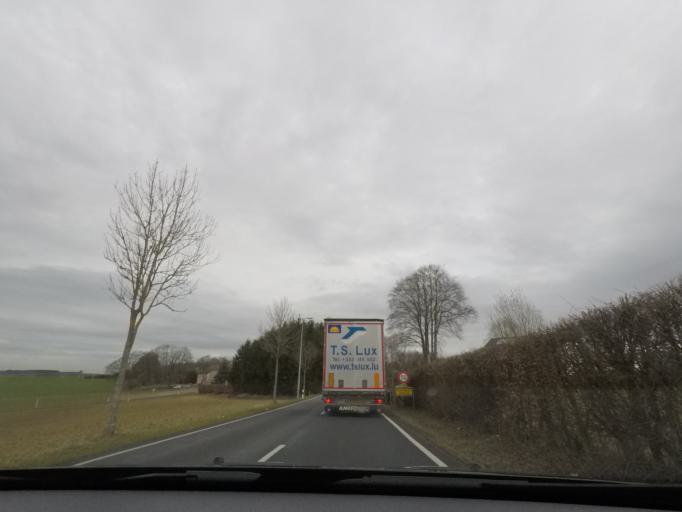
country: LU
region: Diekirch
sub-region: Canton de Wiltz
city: Winseler
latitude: 50.0137
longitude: 5.8820
